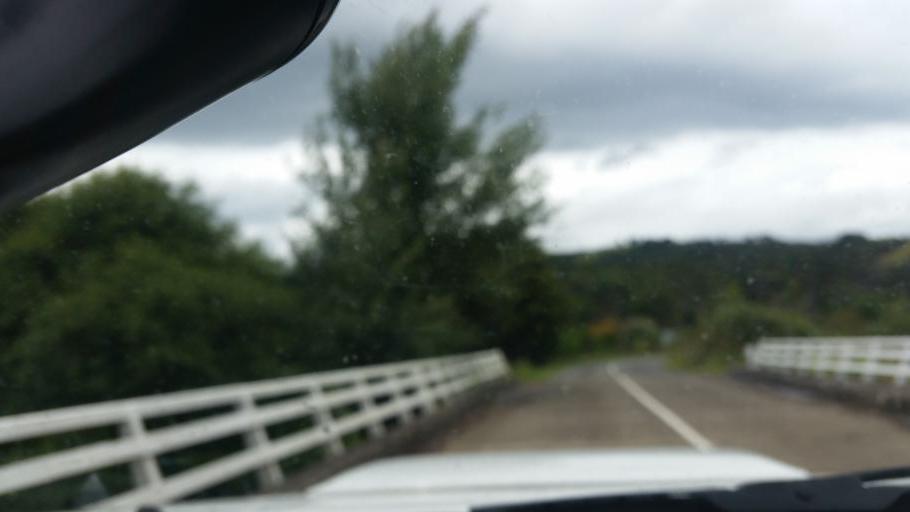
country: NZ
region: Northland
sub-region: Kaipara District
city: Dargaville
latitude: -35.7102
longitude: 173.6188
